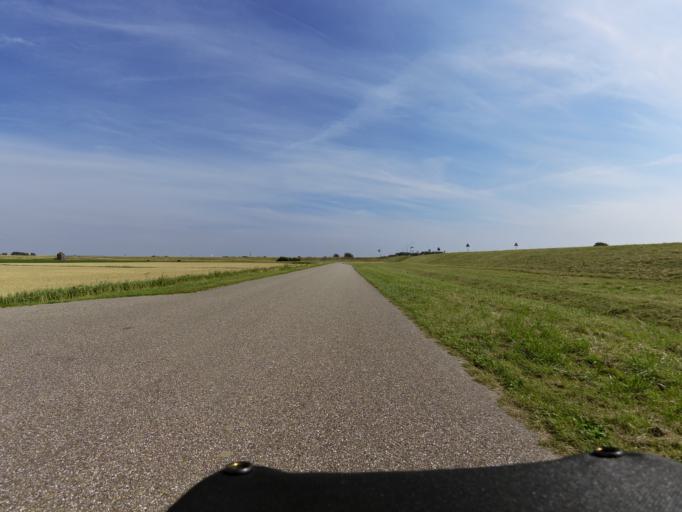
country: NL
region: South Holland
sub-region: Gemeente Goeree-Overflakkee
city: Ouddorp
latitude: 51.7950
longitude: 3.8819
